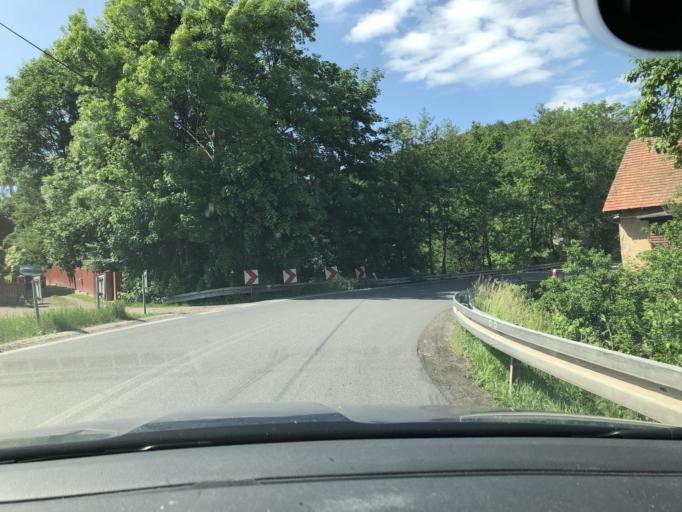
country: PL
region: Lower Silesian Voivodeship
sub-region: Powiat jaworski
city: Bolkow
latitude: 50.9379
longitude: 16.1103
